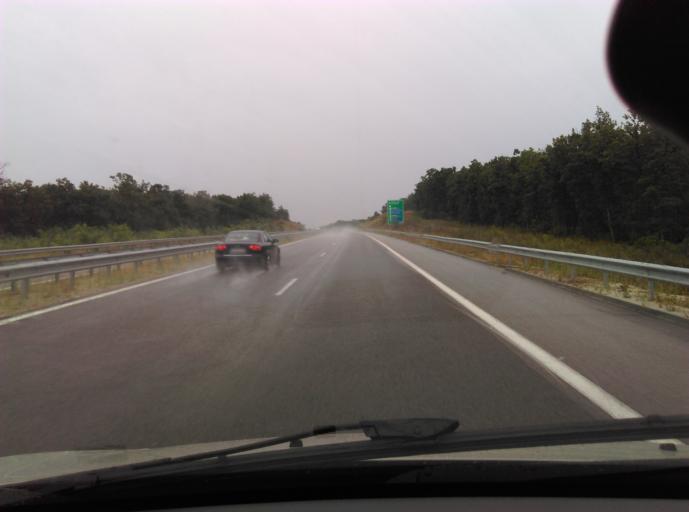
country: BG
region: Khaskovo
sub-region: Obshtina Dimitrovgrad
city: Dimitrovgrad
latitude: 42.0266
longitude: 25.5610
